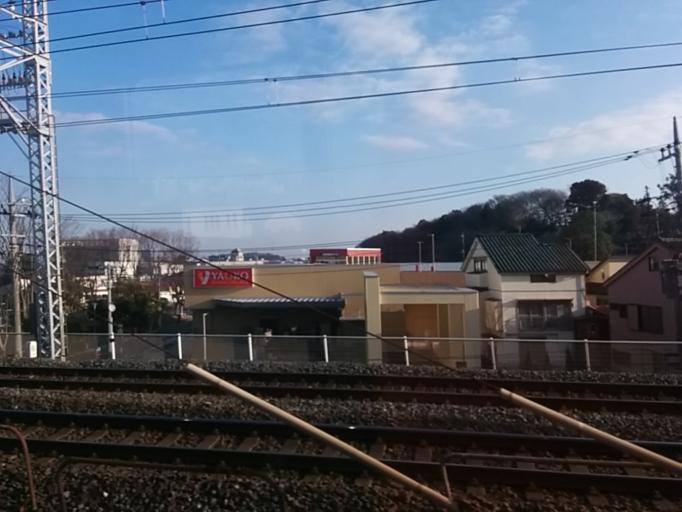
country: JP
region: Saitama
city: Asaka
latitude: 35.8097
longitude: 139.5941
